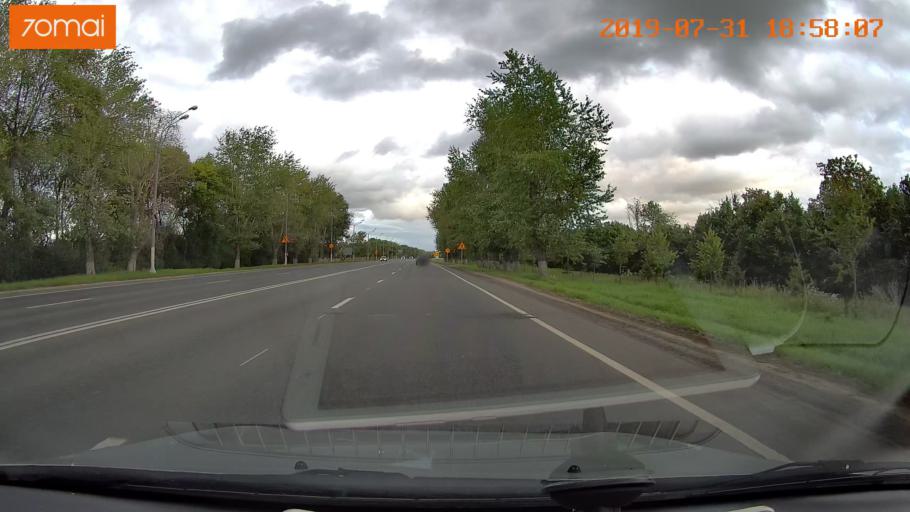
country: RU
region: Moskovskaya
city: Raduzhnyy
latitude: 55.1491
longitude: 38.7005
